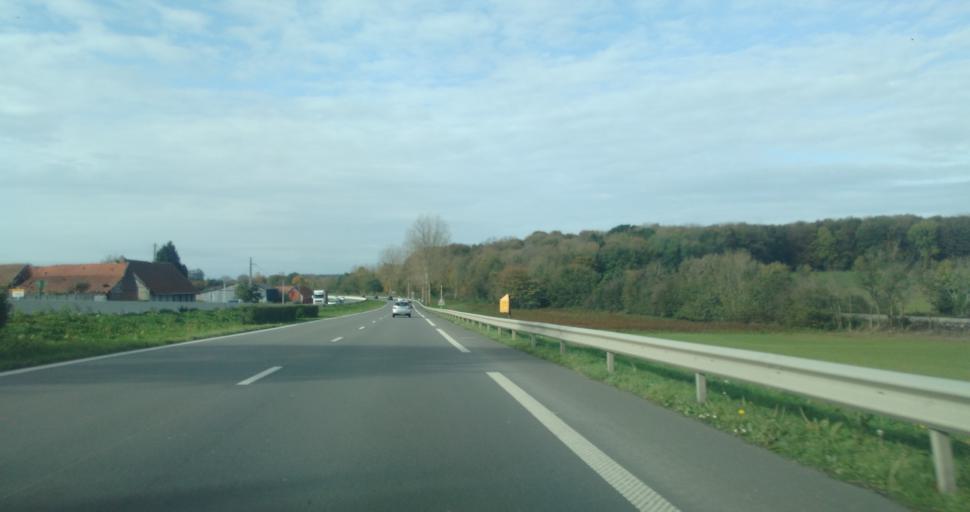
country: FR
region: Nord-Pas-de-Calais
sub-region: Departement du Pas-de-Calais
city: Saint-Pol-sur-Ternoise
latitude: 50.3643
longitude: 2.4372
